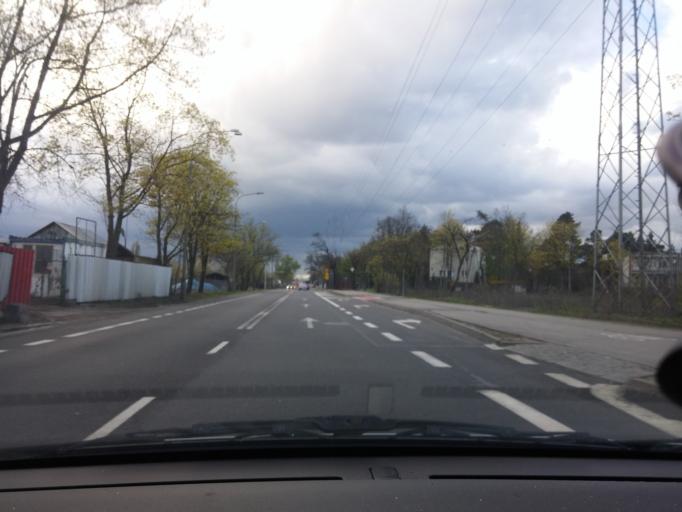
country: PL
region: Masovian Voivodeship
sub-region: Warszawa
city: Wawer
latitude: 52.2218
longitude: 21.1520
